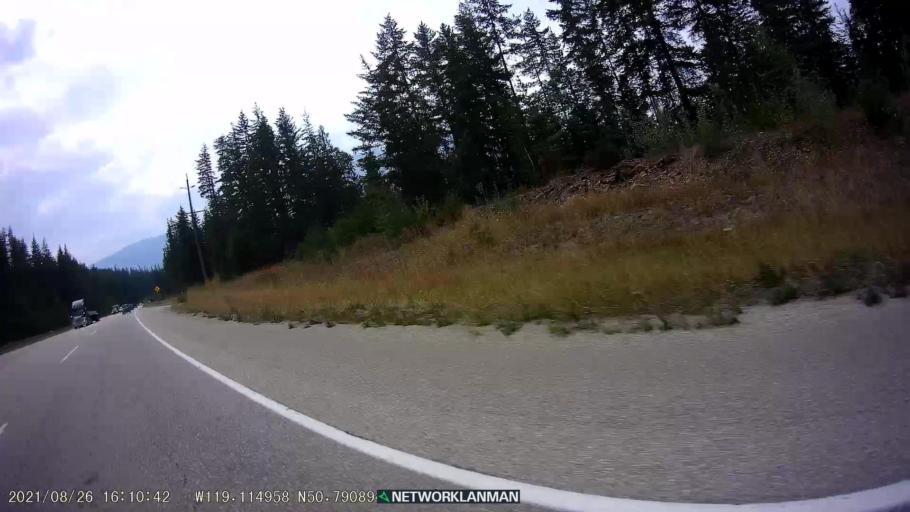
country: CA
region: British Columbia
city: Sicamous
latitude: 50.7904
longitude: -119.1144
